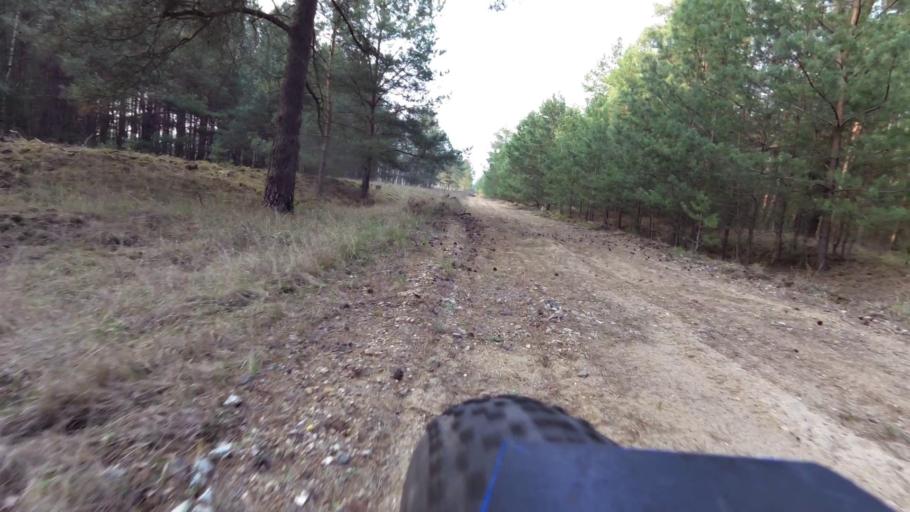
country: DE
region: Brandenburg
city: Vogelsang
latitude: 52.2660
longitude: 14.6918
